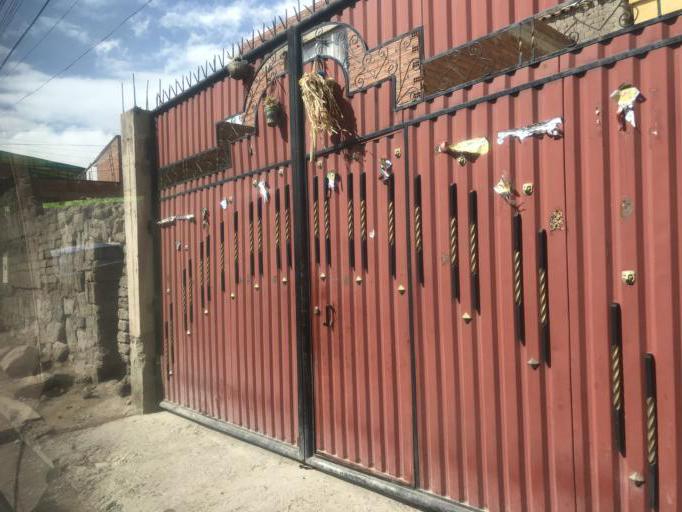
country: BO
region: Potosi
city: Potosi
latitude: -19.6011
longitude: -65.7446
